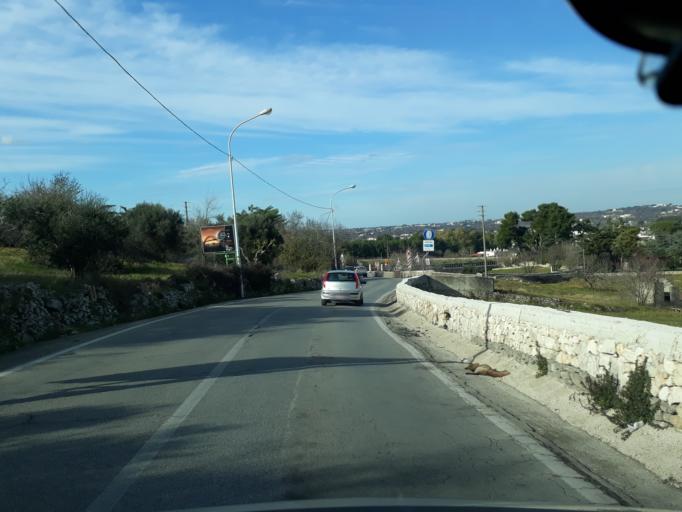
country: IT
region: Apulia
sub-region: Provincia di Taranto
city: Martina Franca
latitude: 40.7115
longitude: 17.3342
